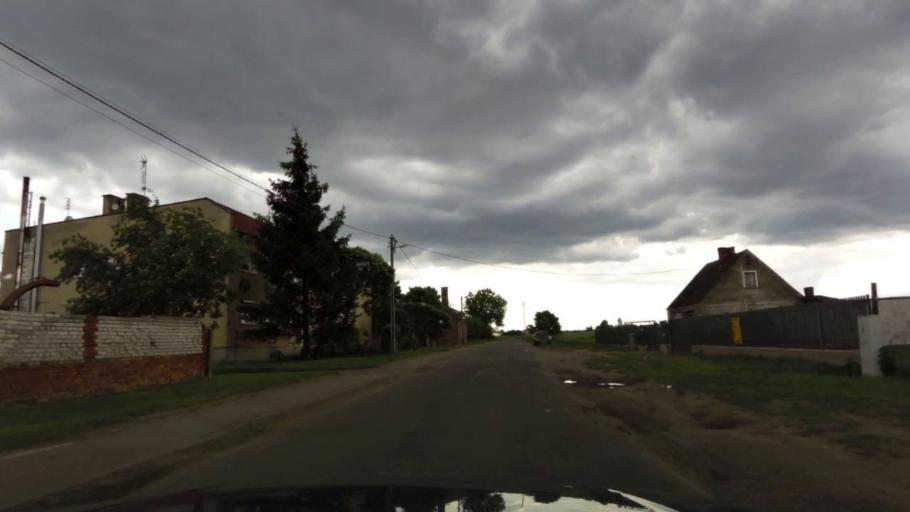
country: PL
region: West Pomeranian Voivodeship
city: Trzcinsko Zdroj
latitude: 52.9610
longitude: 14.6095
